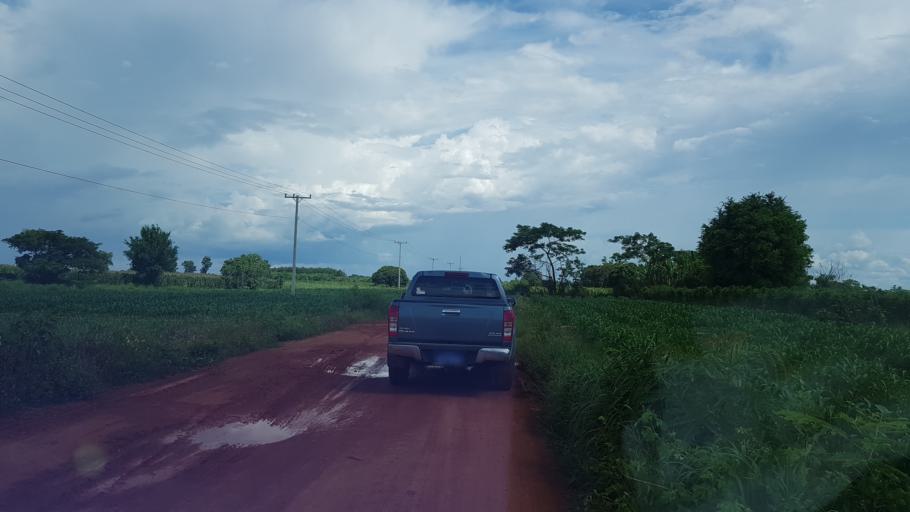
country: LA
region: Vientiane
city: Vientiane
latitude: 18.2312
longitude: 102.5636
